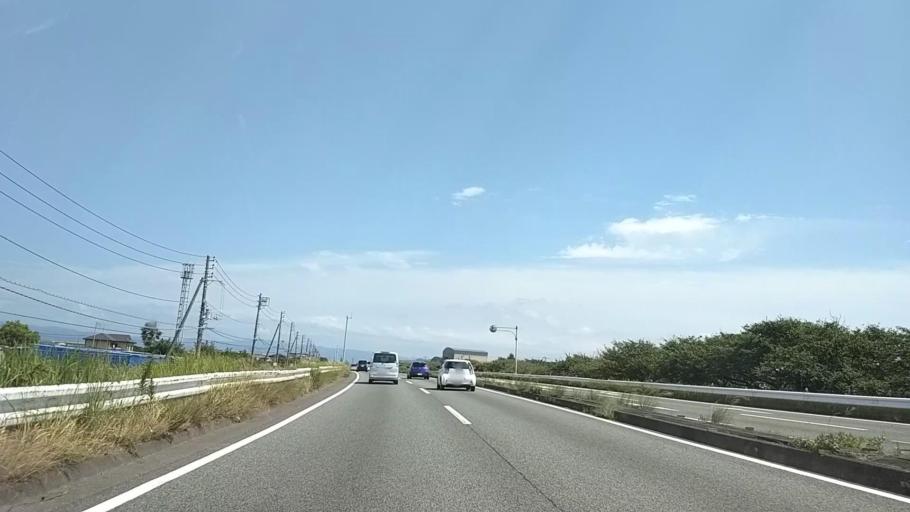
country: JP
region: Shizuoka
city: Numazu
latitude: 35.1311
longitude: 138.7901
